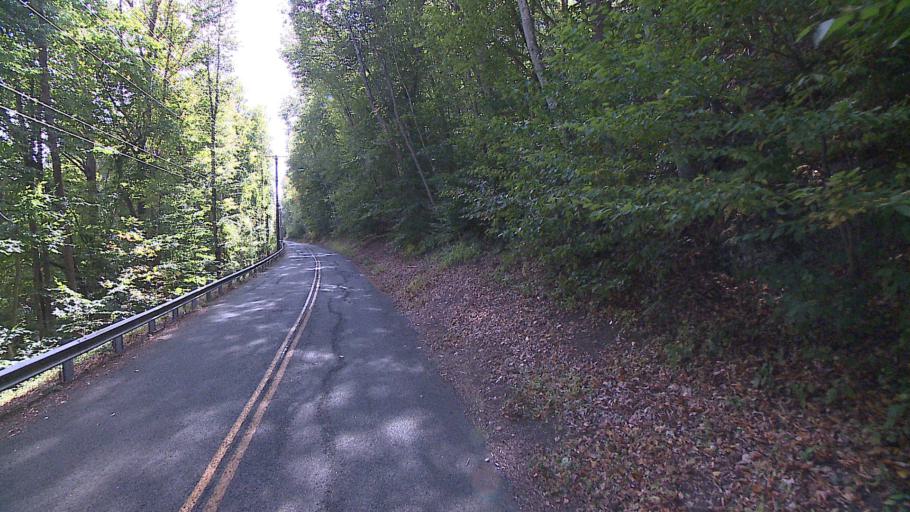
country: US
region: Connecticut
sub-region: Fairfield County
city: Shelton
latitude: 41.3423
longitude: -73.1262
